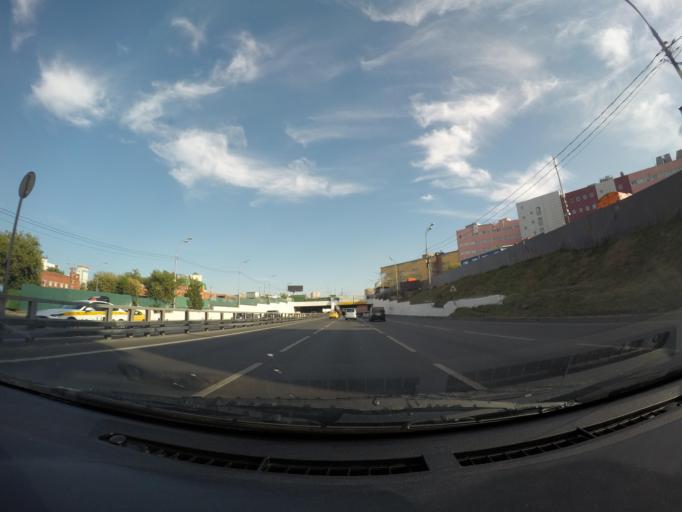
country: RU
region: Moscow
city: Sokol'niki
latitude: 55.7890
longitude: 37.6587
